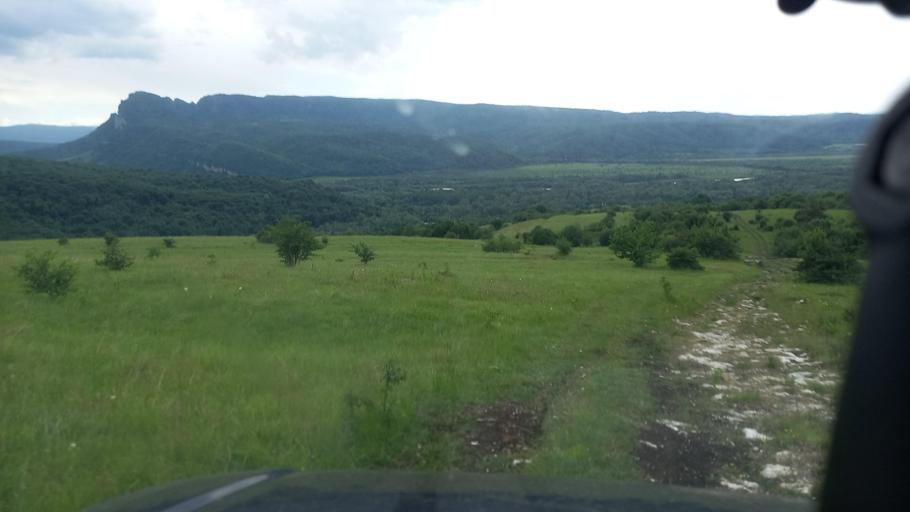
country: RU
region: Karachayevo-Cherkesiya
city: Kurdzhinovo
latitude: 44.1285
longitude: 41.0603
